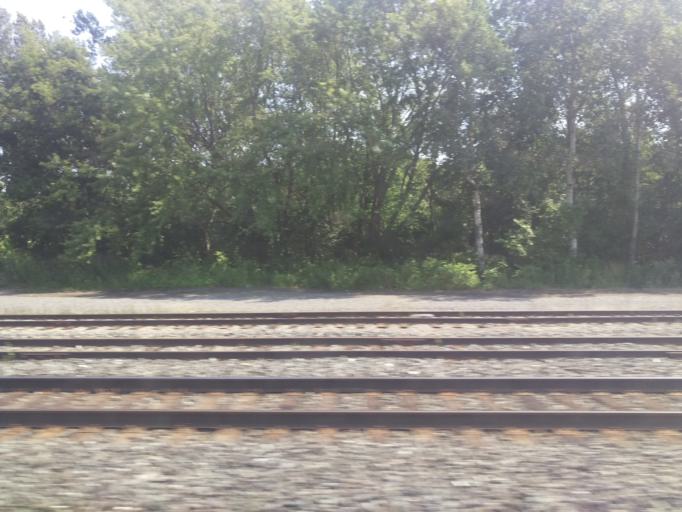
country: CA
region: Ontario
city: Brockville
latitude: 44.5836
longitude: -75.7191
